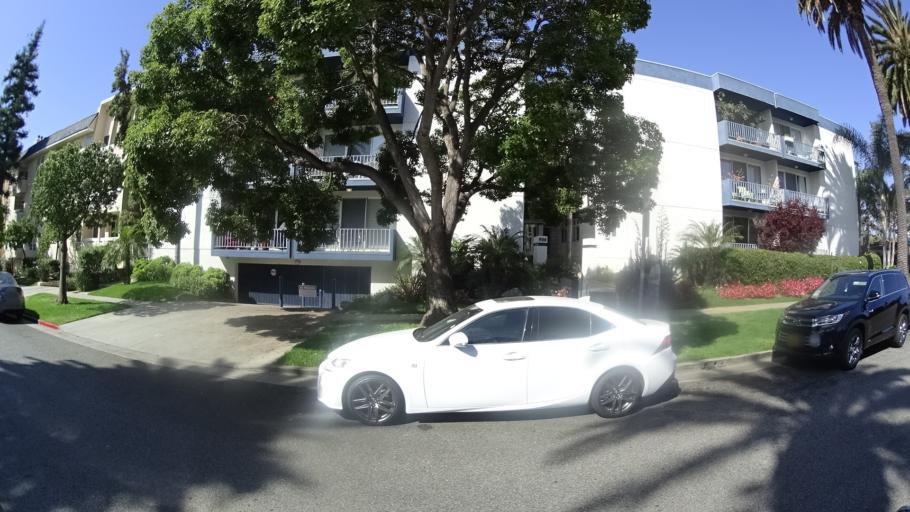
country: US
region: California
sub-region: Los Angeles County
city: Santa Monica
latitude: 34.0298
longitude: -118.4942
